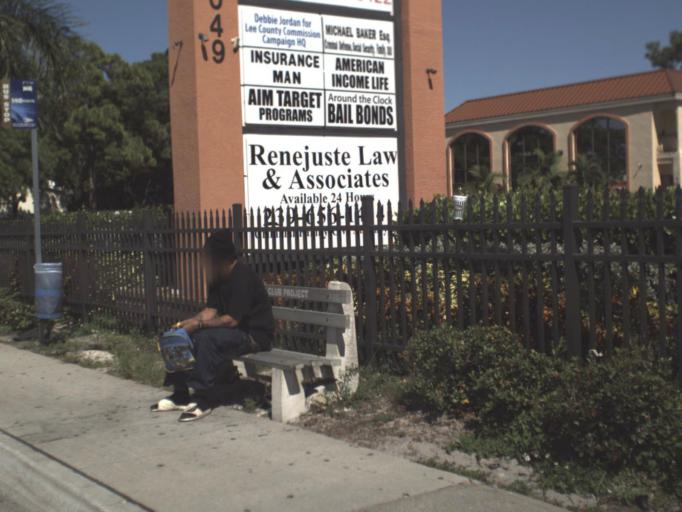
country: US
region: Florida
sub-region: Lee County
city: Fort Myers
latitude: 26.6212
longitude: -81.8721
